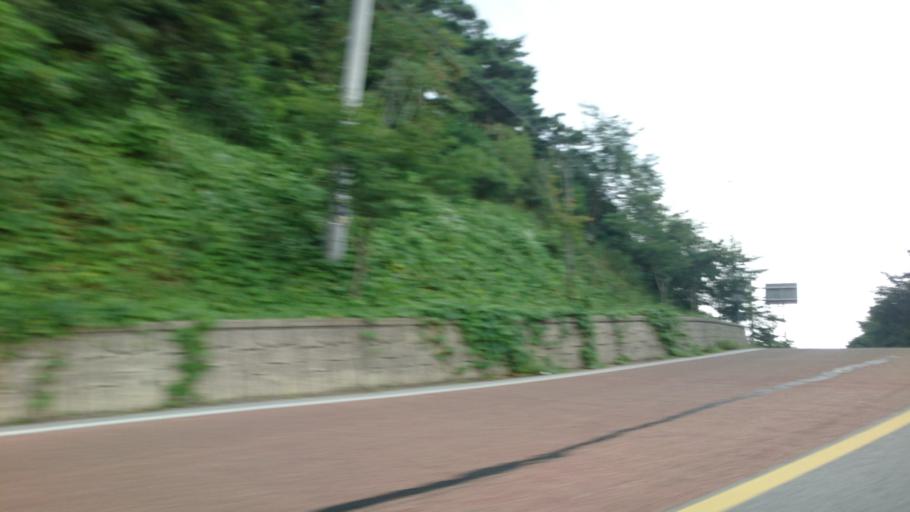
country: KR
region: Daegu
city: Daegu
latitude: 36.0218
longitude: 128.5659
